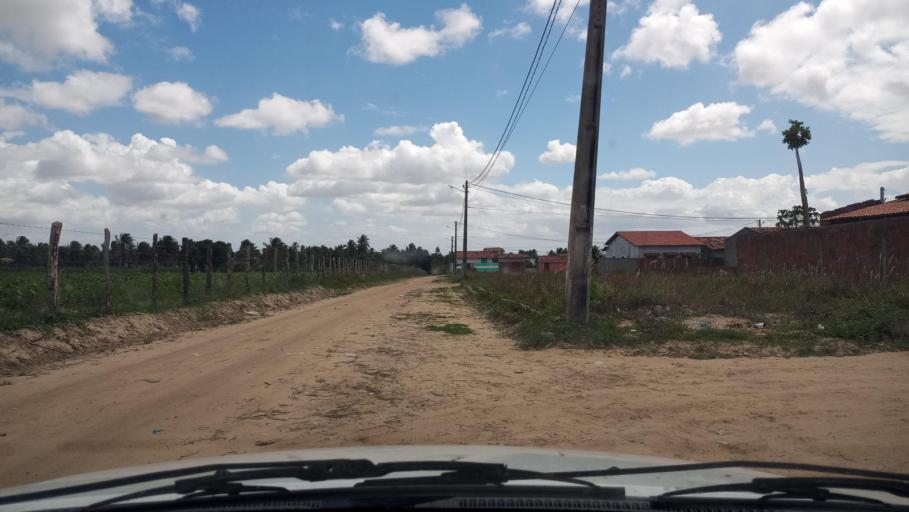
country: BR
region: Rio Grande do Norte
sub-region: Brejinho
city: Brejinho
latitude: -6.1925
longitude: -35.3652
